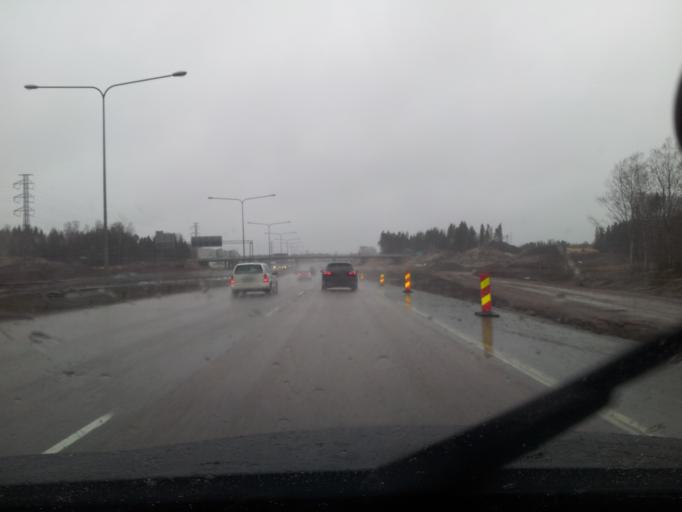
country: FI
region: Uusimaa
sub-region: Helsinki
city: Kilo
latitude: 60.2075
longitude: 24.7902
